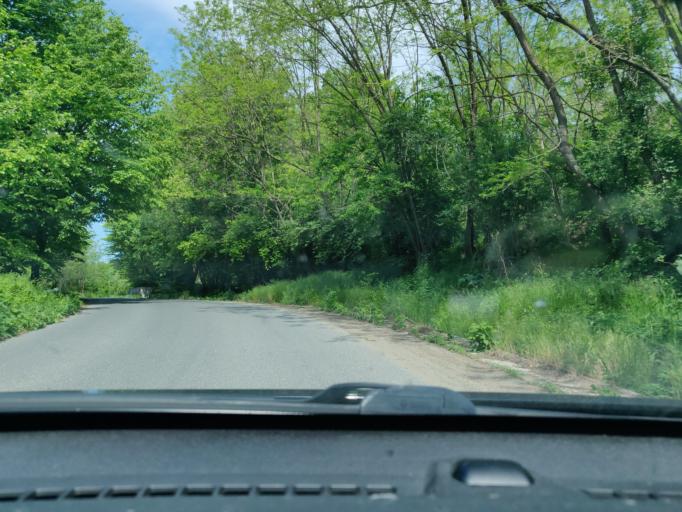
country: RO
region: Vrancea
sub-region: Comuna Vidra
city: Vidra
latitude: 45.9300
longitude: 26.8942
